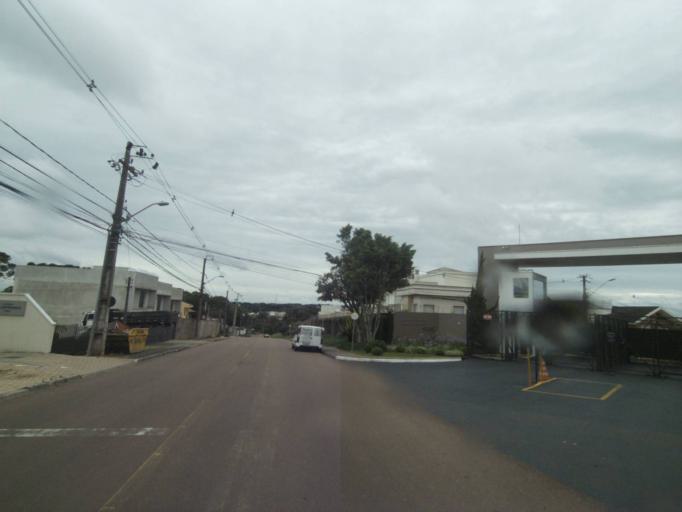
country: BR
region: Parana
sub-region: Curitiba
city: Curitiba
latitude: -25.4581
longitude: -49.3362
